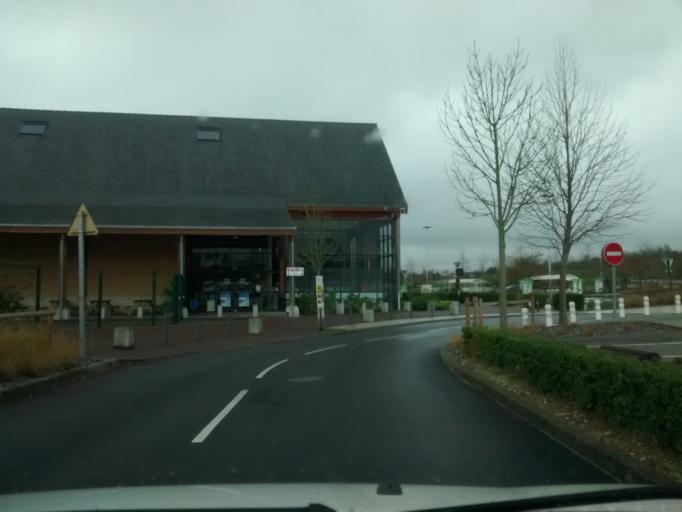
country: FR
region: Brittany
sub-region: Departement d'Ille-et-Vilaine
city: Betton
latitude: 48.1635
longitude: -1.6365
